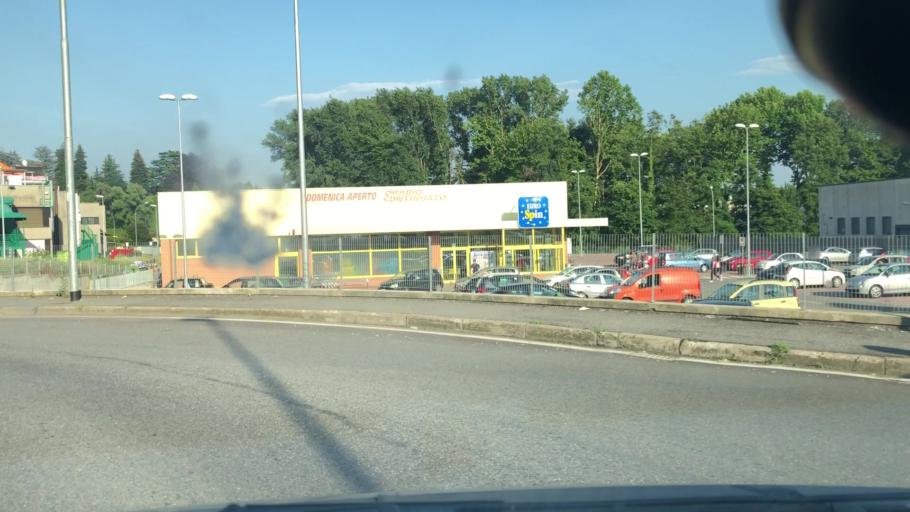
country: IT
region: Lombardy
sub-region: Provincia di Como
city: Villa Guardia
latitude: 45.7715
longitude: 9.0122
